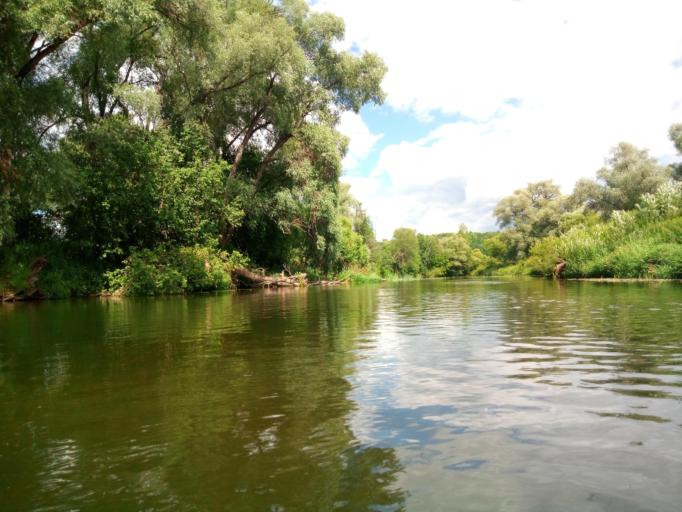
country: RU
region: Kaluga
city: Borovsk
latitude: 55.2107
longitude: 36.3668
